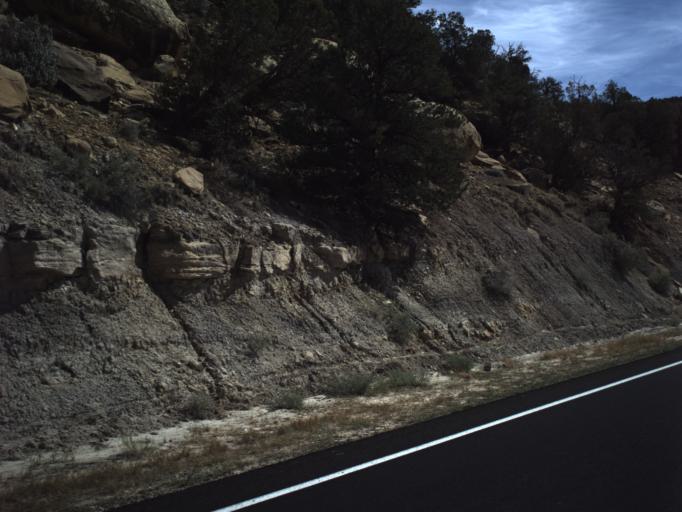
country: US
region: Utah
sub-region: Wayne County
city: Loa
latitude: 37.7412
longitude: -111.7188
